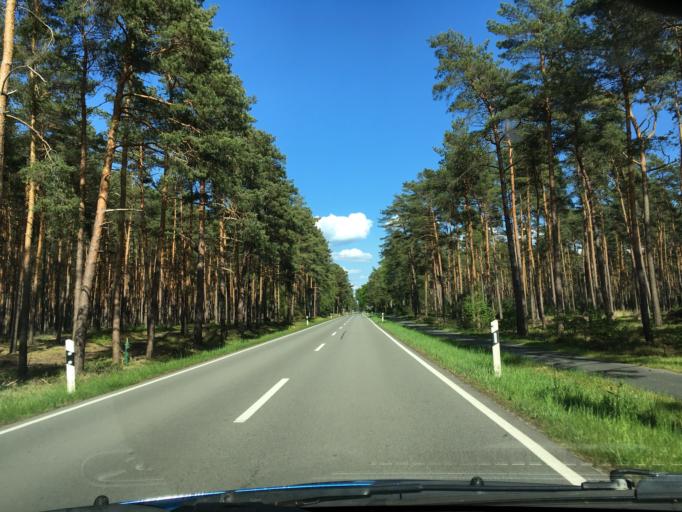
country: DE
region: Lower Saxony
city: Prezelle
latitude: 53.0098
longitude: 11.3842
